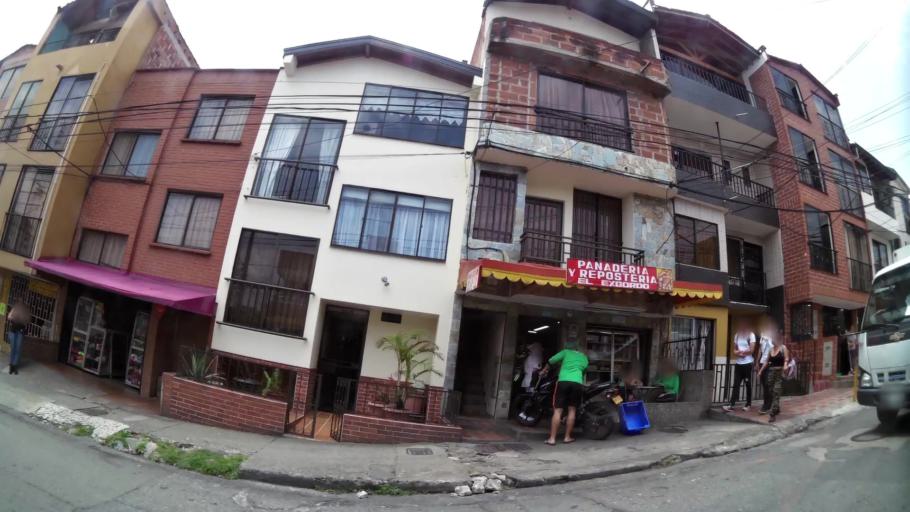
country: CO
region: Antioquia
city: Itagui
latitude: 6.1814
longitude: -75.6034
